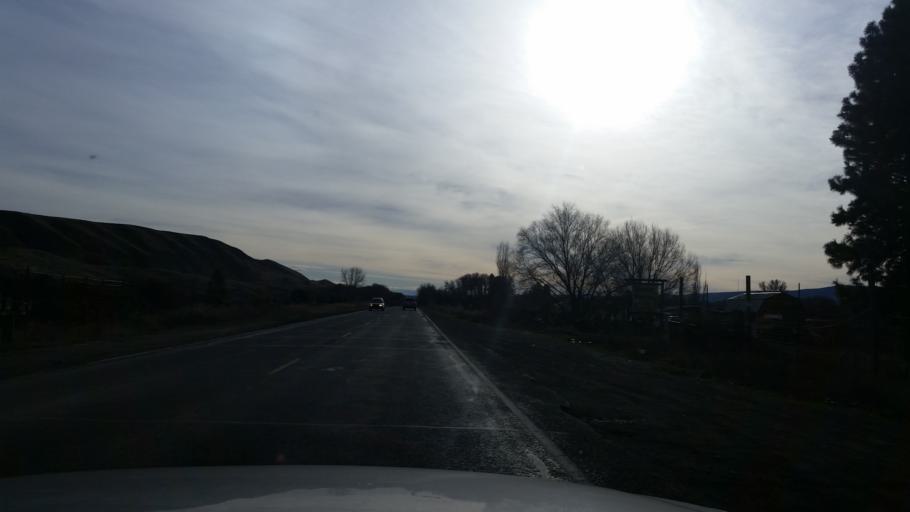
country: US
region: Washington
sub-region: Kittitas County
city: Ellensburg
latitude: 47.0937
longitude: -120.6860
